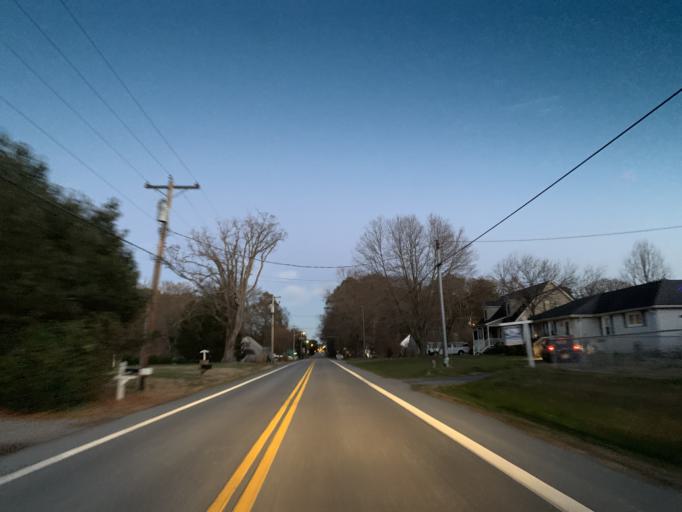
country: US
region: Maryland
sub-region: Kent County
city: Rock Hall
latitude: 39.1395
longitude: -76.2454
